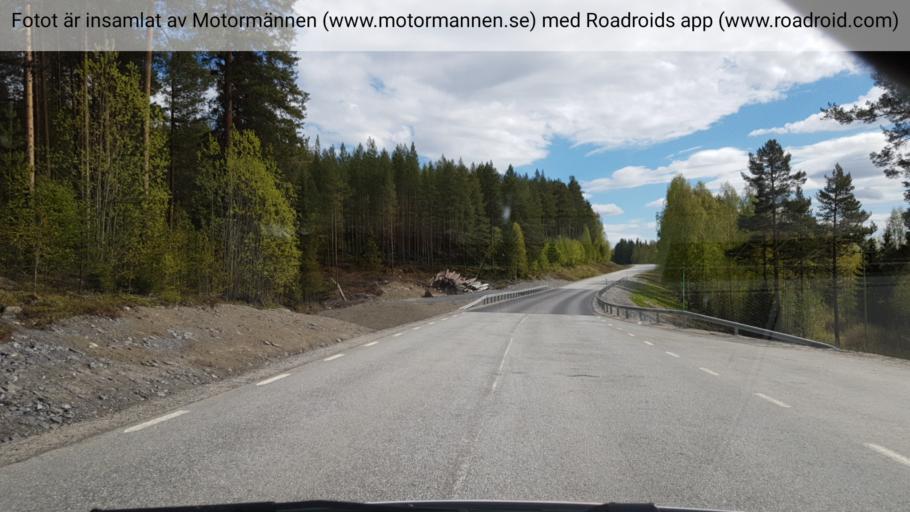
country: SE
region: Vaesterbotten
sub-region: Bjurholms Kommun
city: Bjurholm
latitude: 64.2726
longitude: 19.2622
